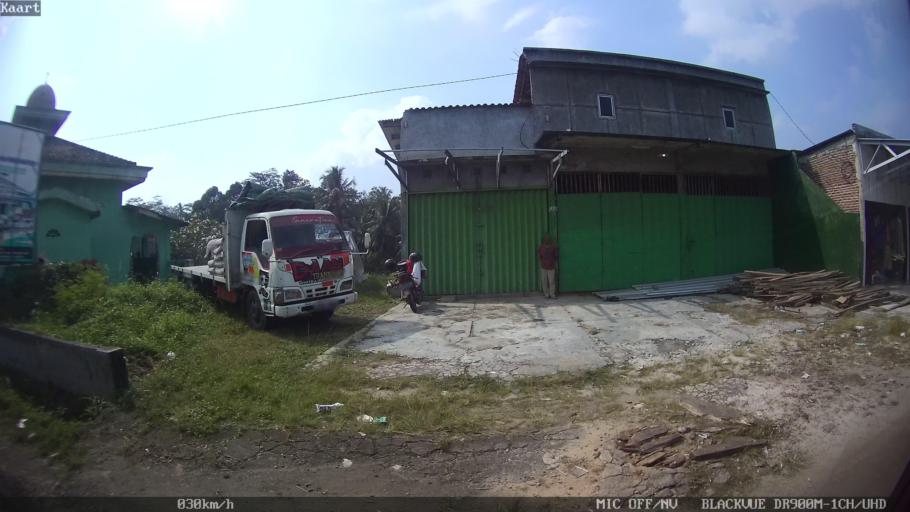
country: ID
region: Lampung
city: Natar
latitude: -5.3640
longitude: 105.1852
